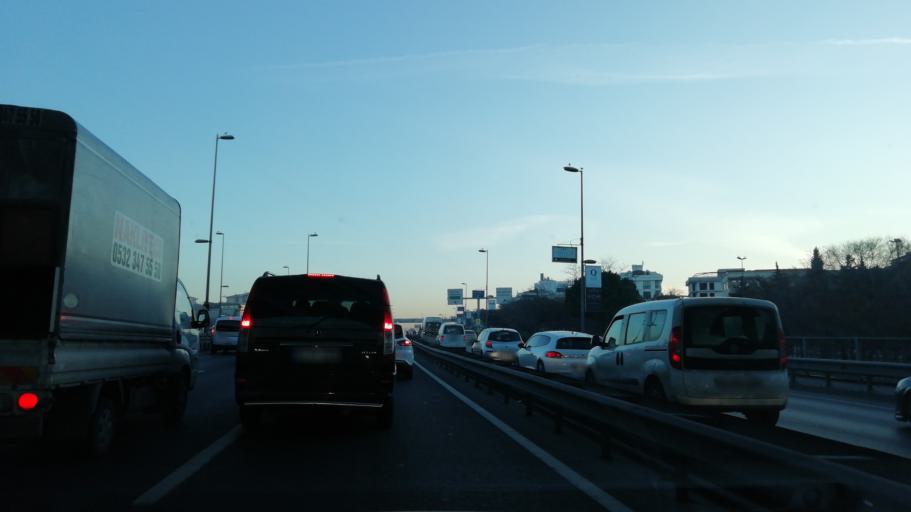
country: TR
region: Istanbul
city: Bahcelievler
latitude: 40.9970
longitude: 28.8697
